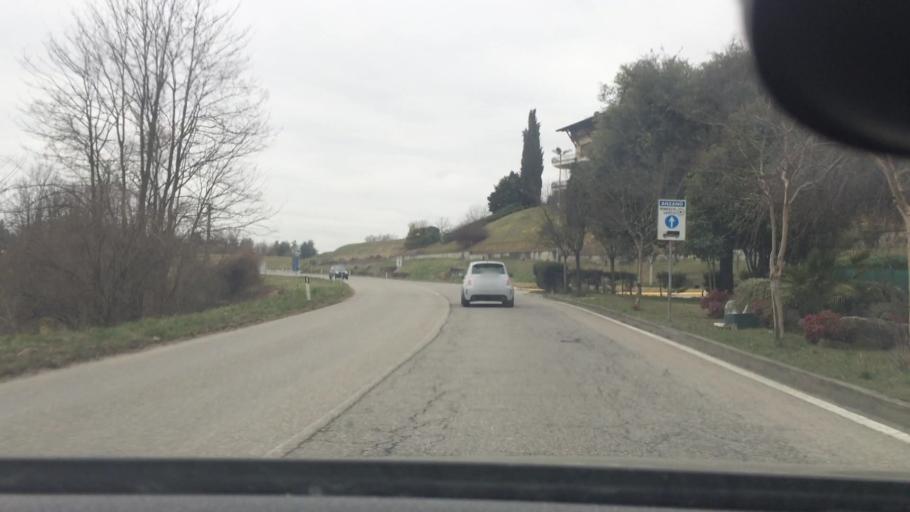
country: IT
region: Lombardy
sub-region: Provincia di Como
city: Nobile-Monguzzo
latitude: 45.7776
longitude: 9.2316
